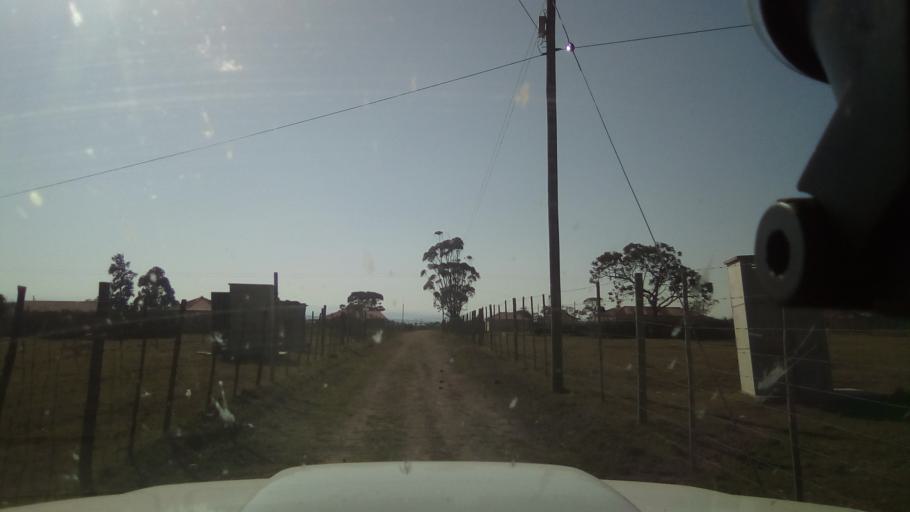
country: ZA
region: Eastern Cape
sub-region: Buffalo City Metropolitan Municipality
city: Bhisho
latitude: -32.9424
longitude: 27.3330
